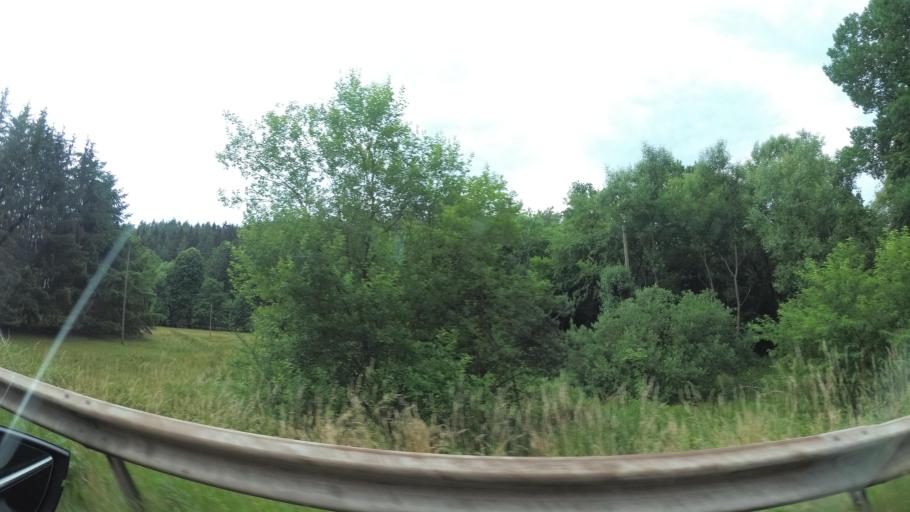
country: DE
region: Rheinland-Pfalz
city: Fischbach
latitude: 49.4693
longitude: 7.9162
